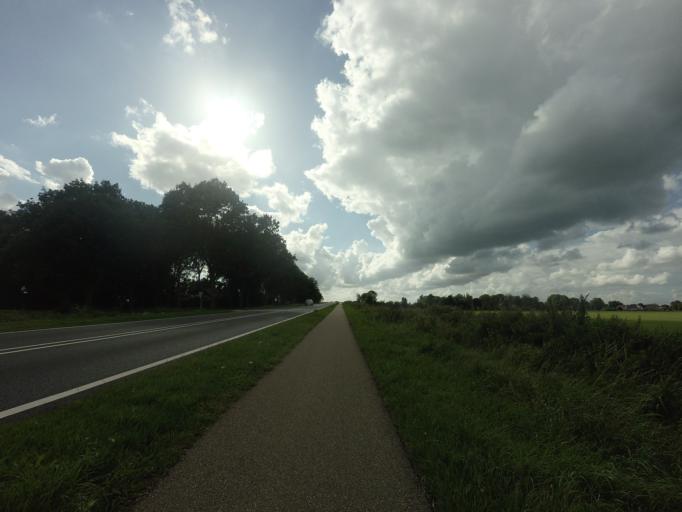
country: NL
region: Overijssel
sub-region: Gemeente Steenwijkerland
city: Blokzijl
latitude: 52.7449
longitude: 6.0017
